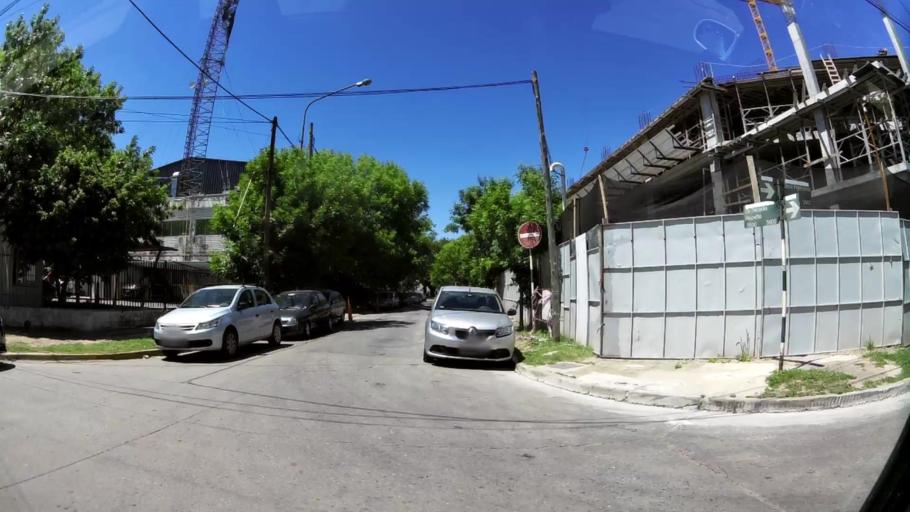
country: AR
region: Buenos Aires
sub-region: Partido de Vicente Lopez
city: Olivos
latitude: -34.5142
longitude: -58.5181
